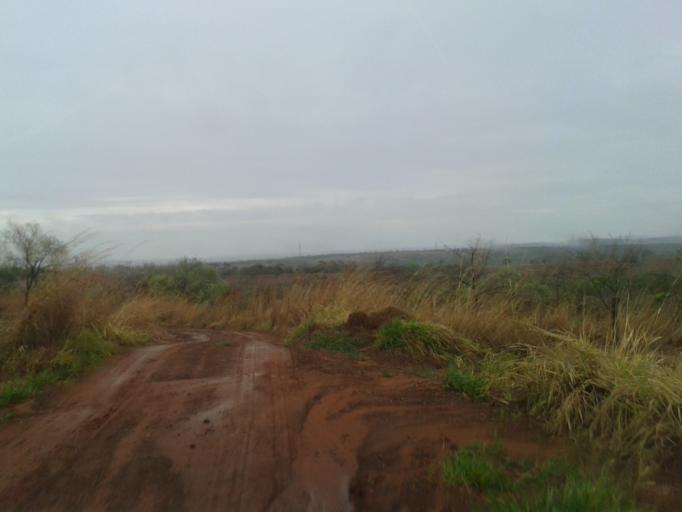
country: BR
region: Minas Gerais
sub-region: Campina Verde
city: Campina Verde
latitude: -19.3218
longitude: -49.5126
